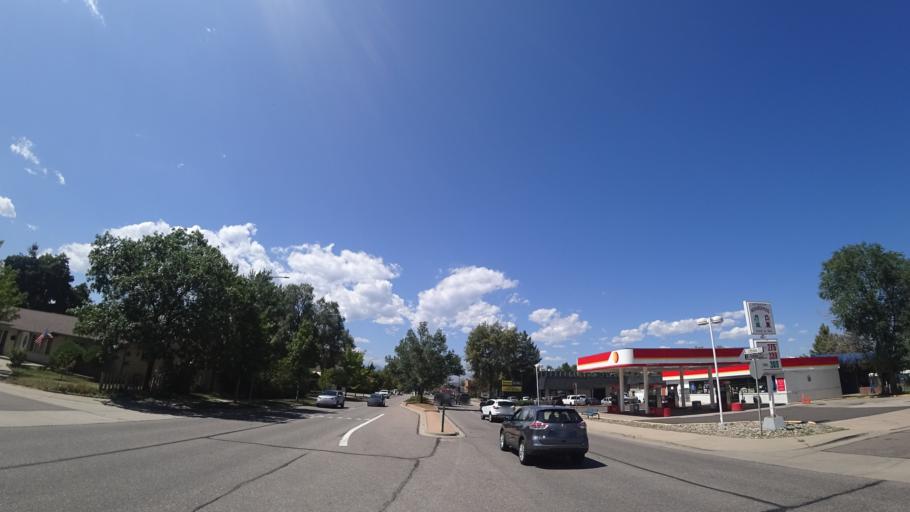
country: US
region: Colorado
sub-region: Arapahoe County
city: Littleton
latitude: 39.6132
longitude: -104.9990
